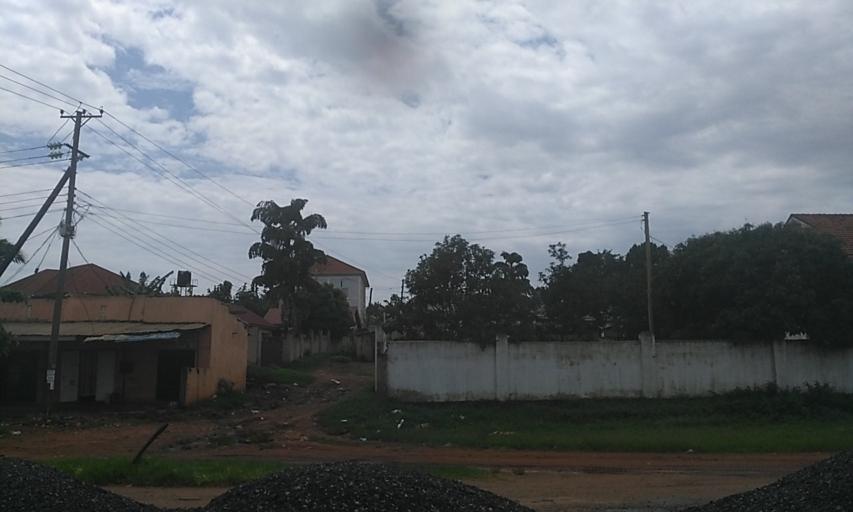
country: UG
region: Central Region
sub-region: Wakiso District
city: Kireka
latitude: 0.3692
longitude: 32.6287
